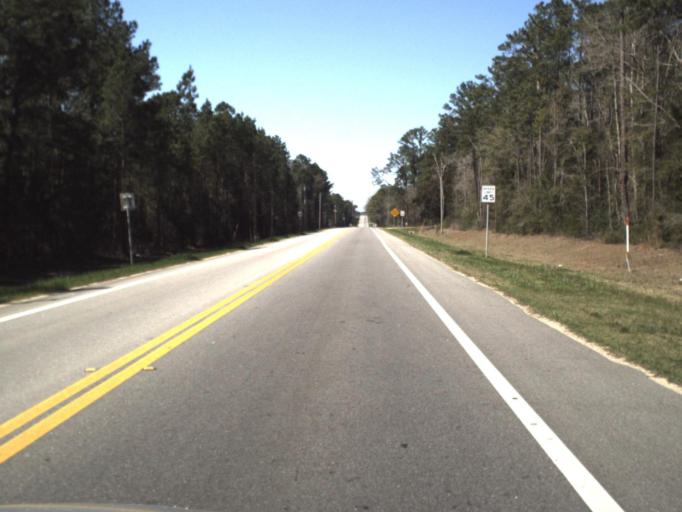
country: US
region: Florida
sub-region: Jackson County
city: Marianna
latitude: 30.7890
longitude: -85.2607
